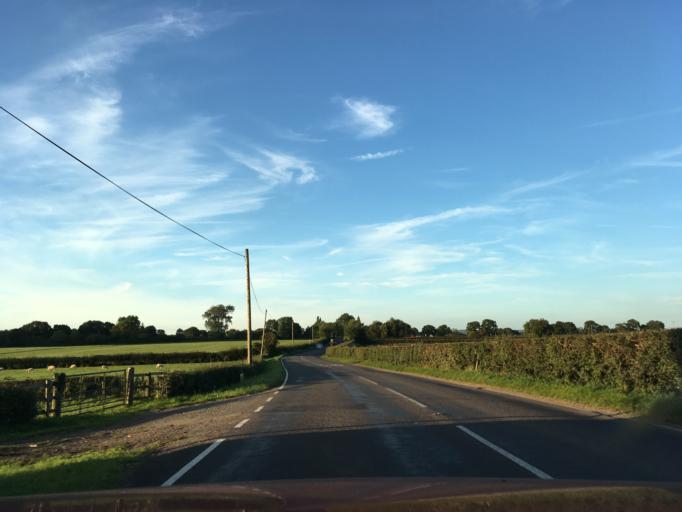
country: GB
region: England
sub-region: South Gloucestershire
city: Tytherington
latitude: 51.5943
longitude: -2.4450
